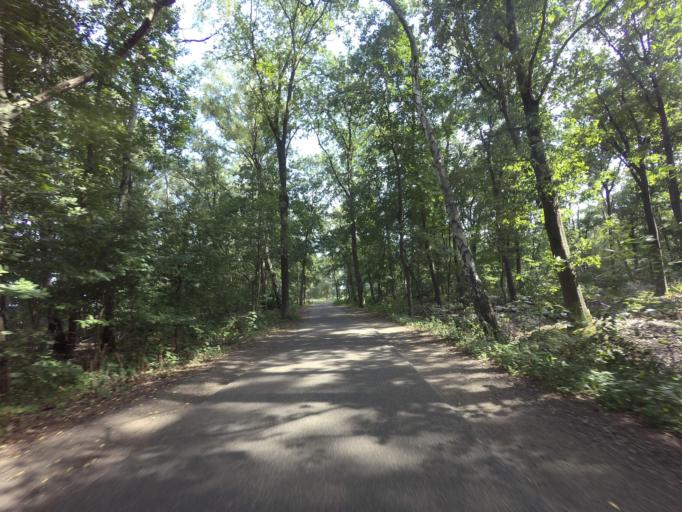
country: NL
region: North Brabant
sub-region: Gemeente Someren
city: Someren
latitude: 51.3990
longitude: 5.6776
